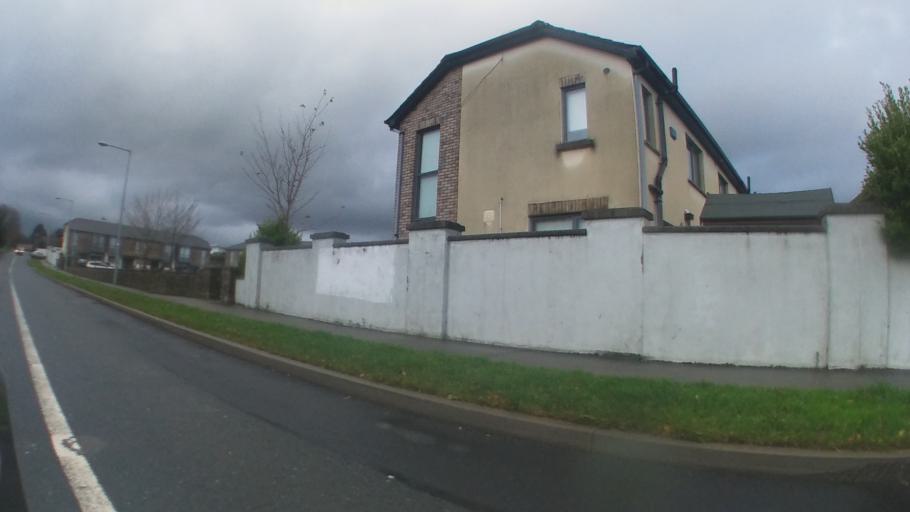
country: IE
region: Leinster
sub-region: Wicklow
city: Kilcoole
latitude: 53.1039
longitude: -6.0668
